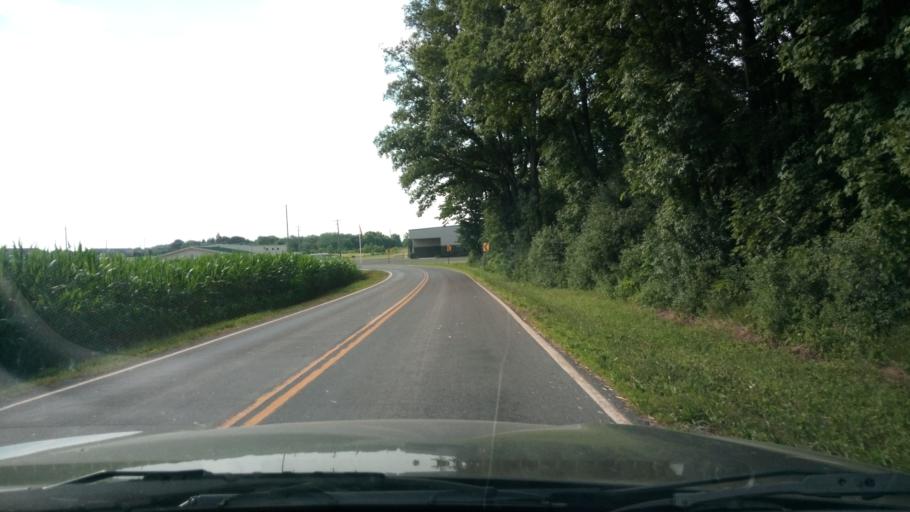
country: US
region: New York
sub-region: Wayne County
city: Lyons
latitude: 43.0439
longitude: -76.9796
